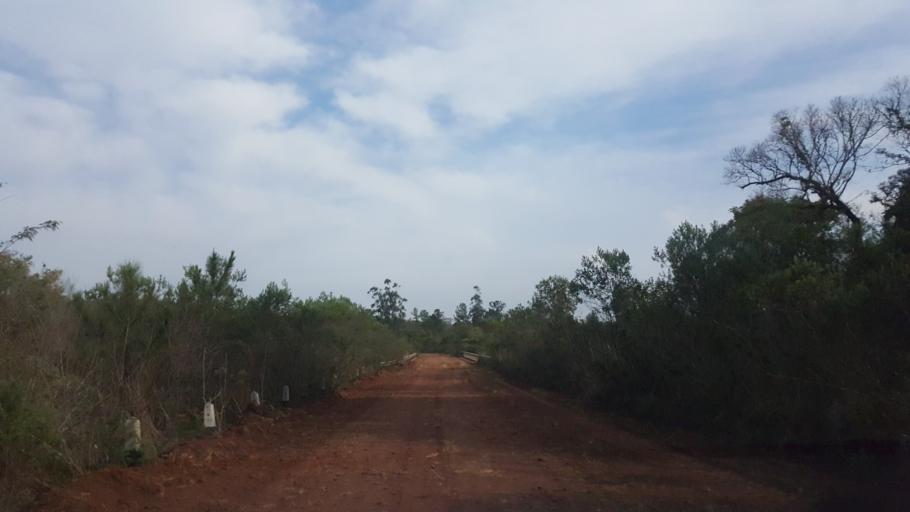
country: AR
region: Misiones
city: Capiovi
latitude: -26.9035
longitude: -55.1081
